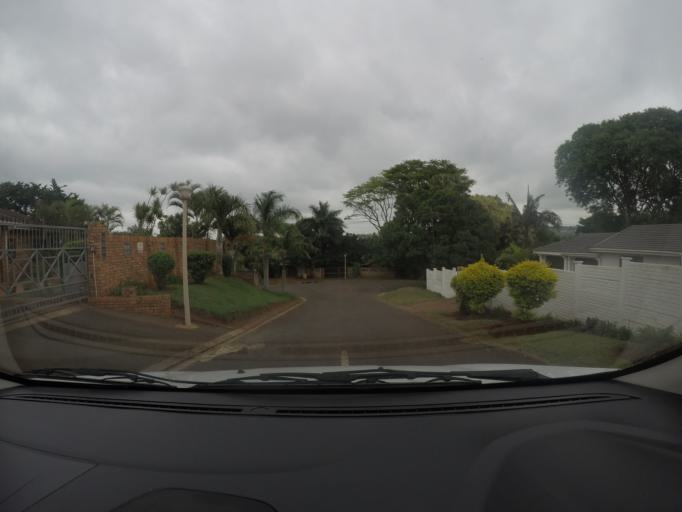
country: ZA
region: KwaZulu-Natal
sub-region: uThungulu District Municipality
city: Empangeni
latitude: -28.7649
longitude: 31.8876
